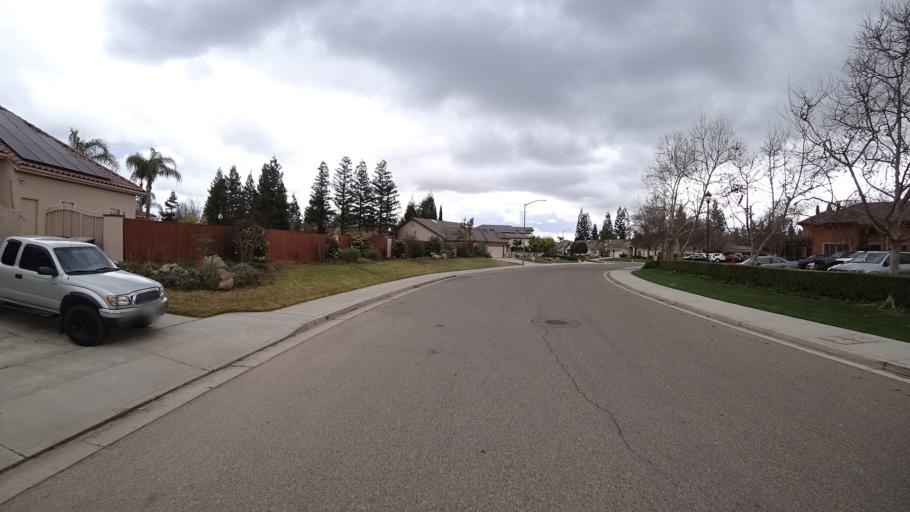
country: US
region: California
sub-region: Fresno County
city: Fresno
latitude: 36.8386
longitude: -119.8350
